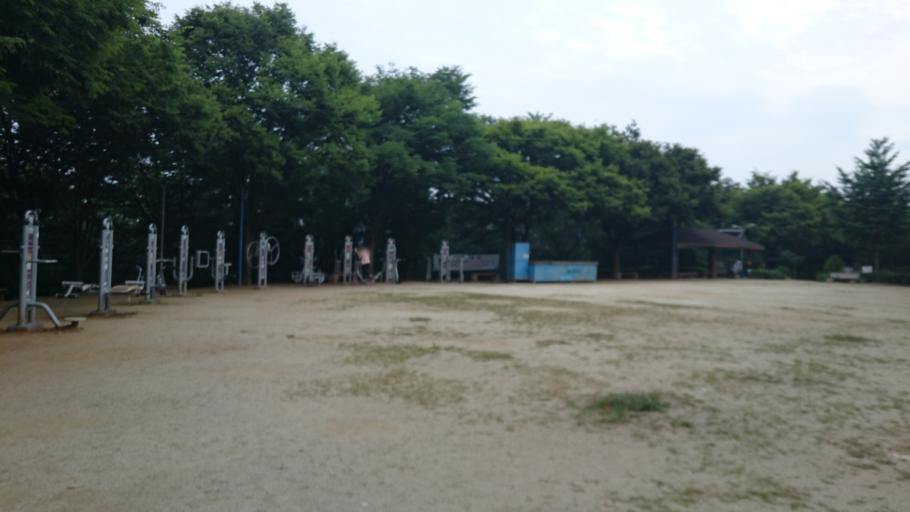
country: KR
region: Daegu
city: Daegu
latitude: 35.8647
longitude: 128.6326
